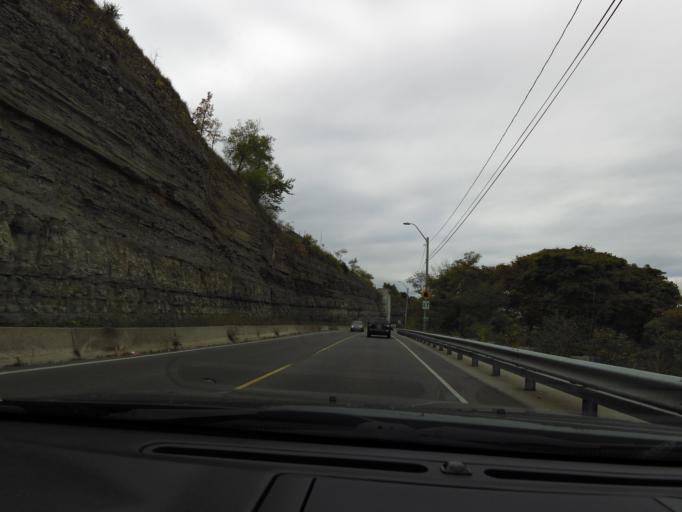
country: CA
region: Ontario
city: Hamilton
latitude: 43.2407
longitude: -79.8437
